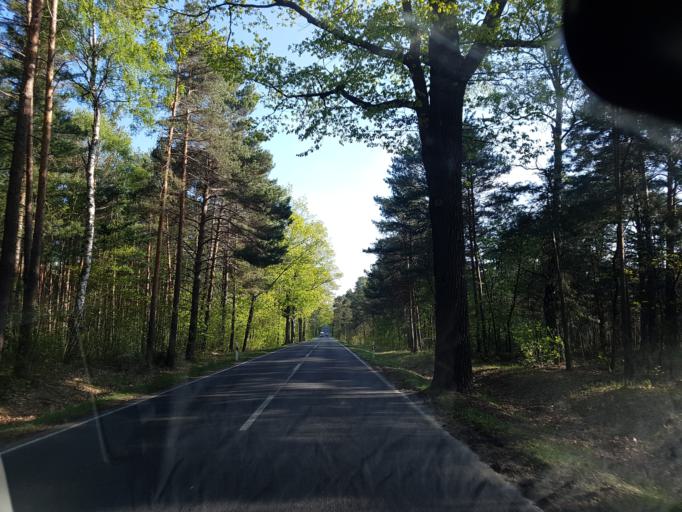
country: DE
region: Brandenburg
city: Altdobern
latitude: 51.6188
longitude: 14.0240
